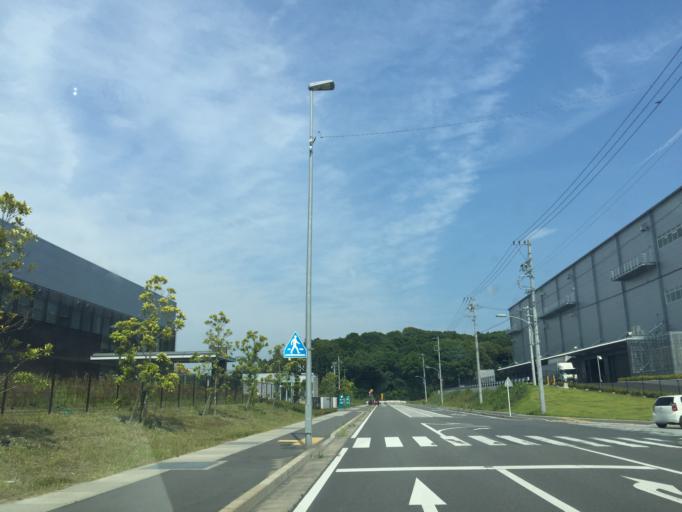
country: JP
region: Shizuoka
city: Kakegawa
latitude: 34.7582
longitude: 138.0021
